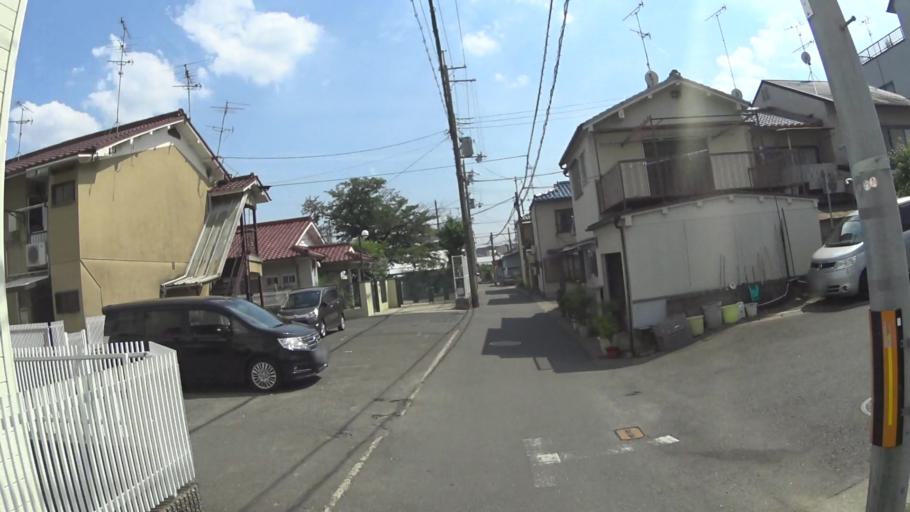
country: JP
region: Kyoto
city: Muko
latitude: 35.0064
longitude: 135.6942
